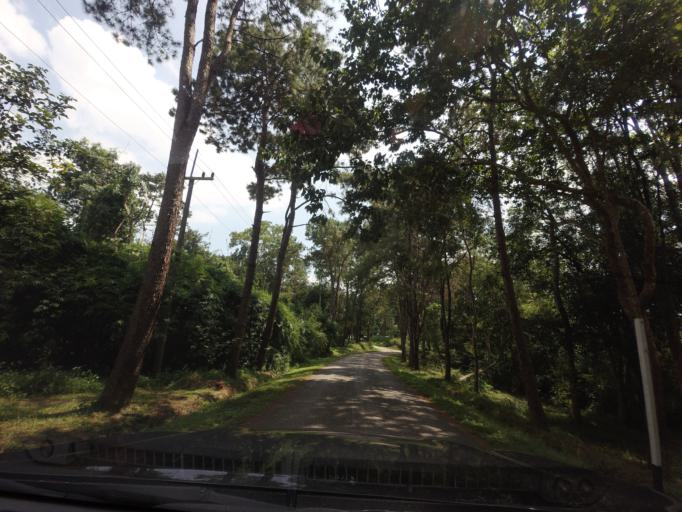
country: TH
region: Loei
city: Phu Ruea
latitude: 17.4806
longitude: 101.3522
